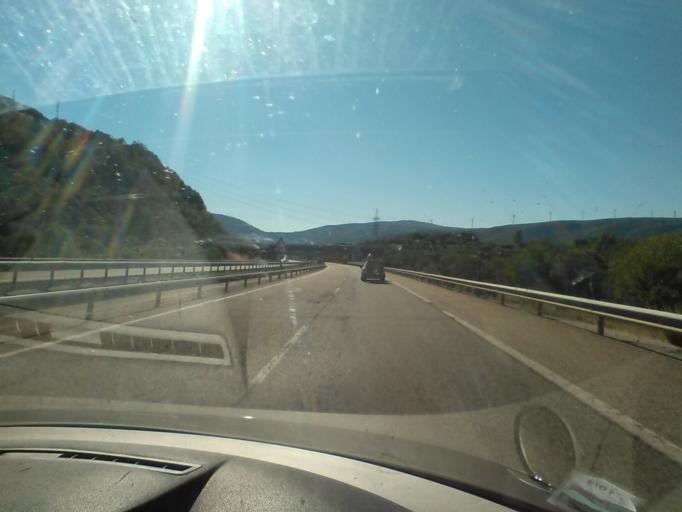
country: ES
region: Castille and Leon
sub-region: Provincia de Zamora
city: Lubian
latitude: 42.0357
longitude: -6.8575
